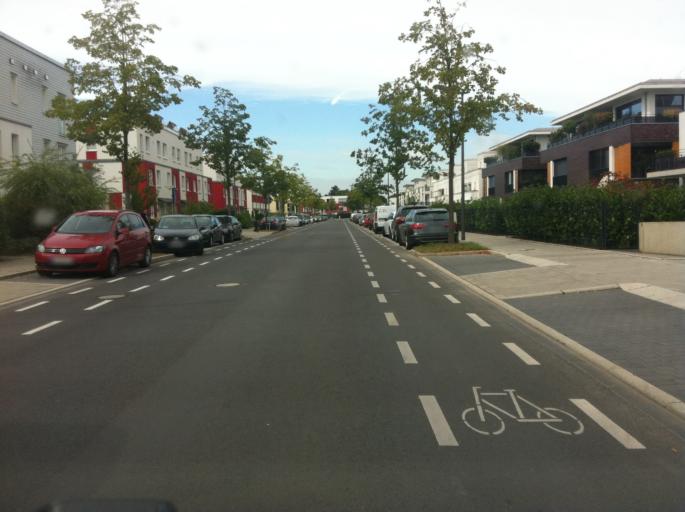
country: DE
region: North Rhine-Westphalia
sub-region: Regierungsbezirk Koln
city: Mengenich
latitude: 50.9651
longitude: 6.8424
